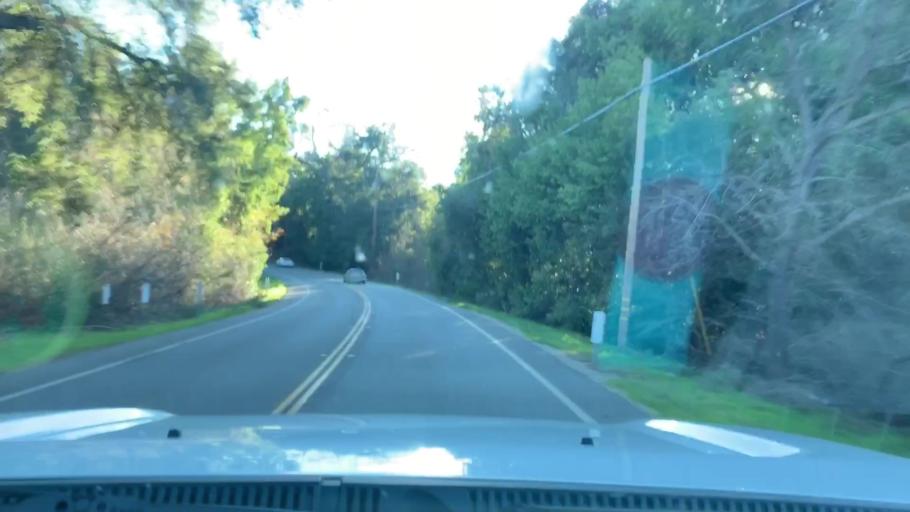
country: US
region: California
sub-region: San Luis Obispo County
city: Atascadero
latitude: 35.4574
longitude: -120.7504
